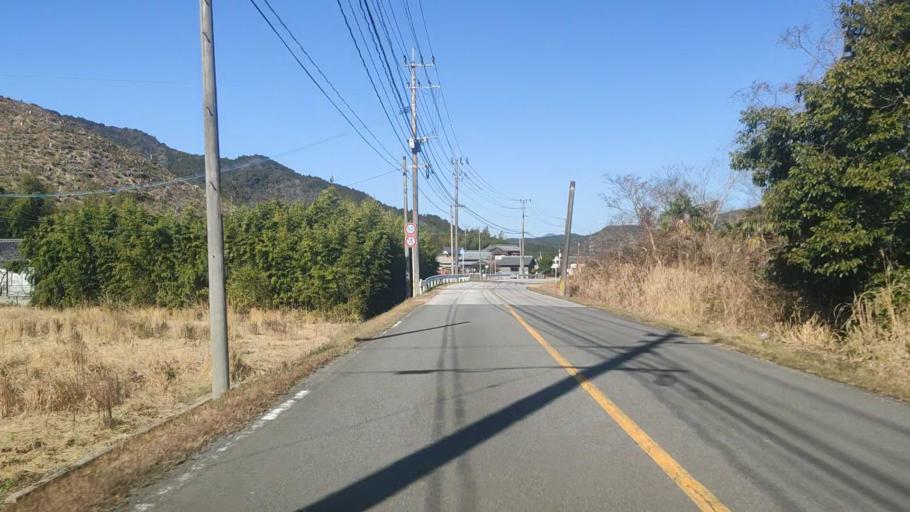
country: JP
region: Oita
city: Saiki
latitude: 32.9133
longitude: 131.9289
